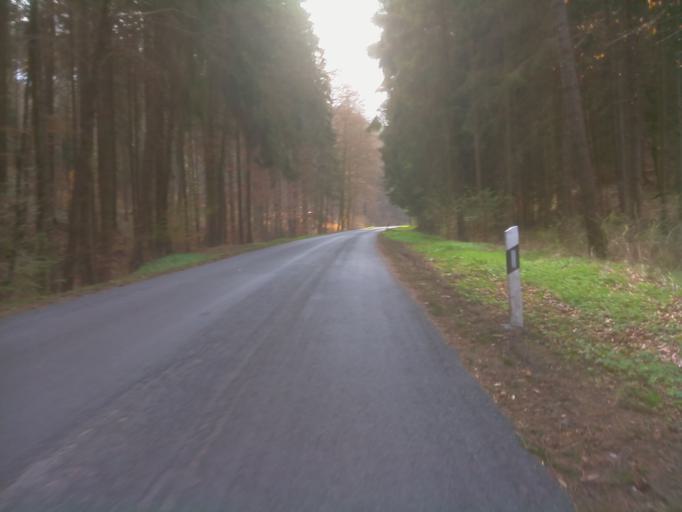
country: DE
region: Thuringia
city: Grosseutersdorf
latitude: 50.7728
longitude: 11.5631
